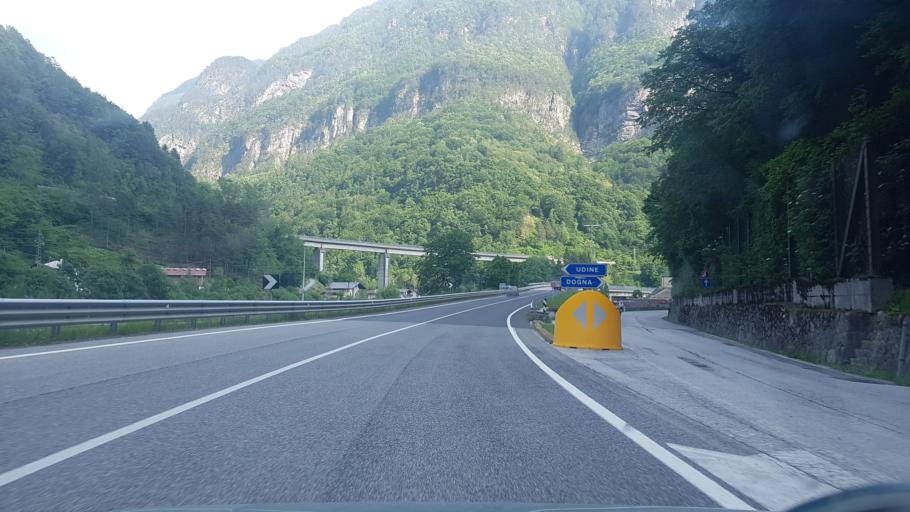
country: IT
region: Friuli Venezia Giulia
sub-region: Provincia di Udine
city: Dogna
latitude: 46.4510
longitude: 13.3144
